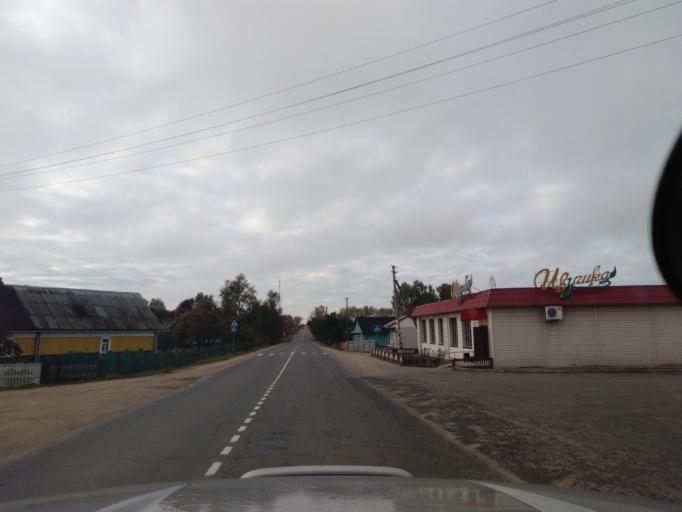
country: BY
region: Minsk
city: Kapyl'
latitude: 53.1582
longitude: 27.0775
